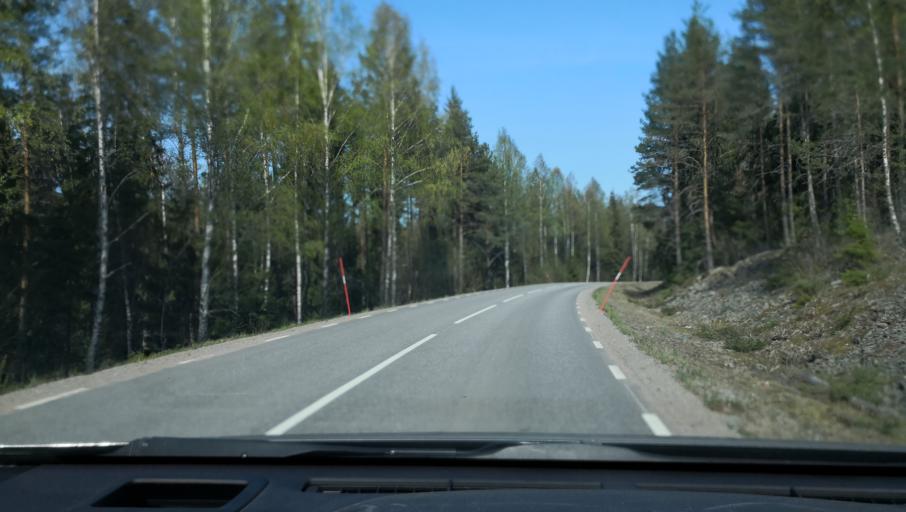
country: SE
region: Vaestmanland
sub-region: Sala Kommun
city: Sala
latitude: 59.9934
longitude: 16.6478
